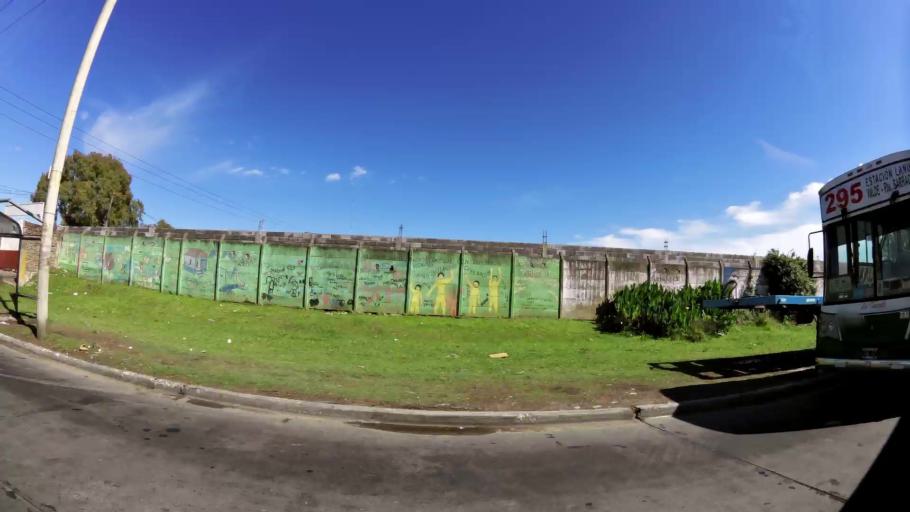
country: AR
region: Buenos Aires
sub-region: Partido de Avellaneda
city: Avellaneda
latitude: -34.6868
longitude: -58.3110
